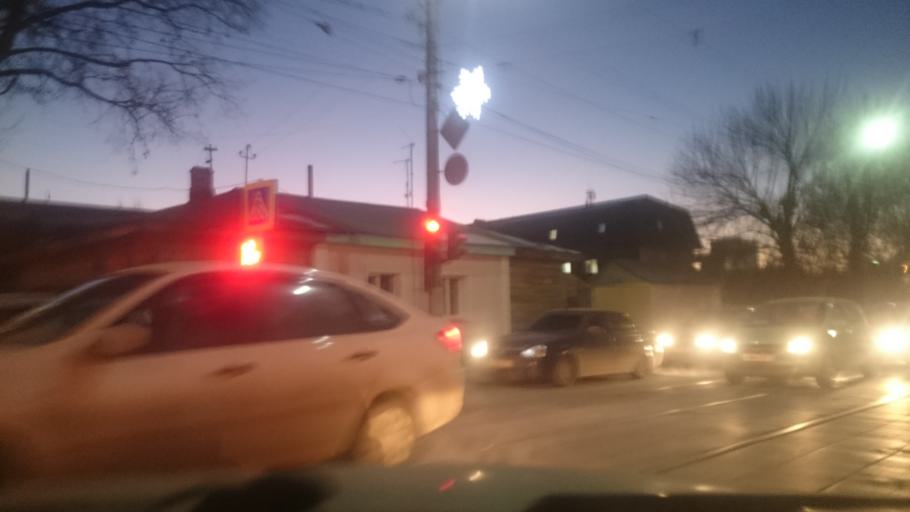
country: RU
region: Tula
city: Tula
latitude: 54.1997
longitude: 37.6334
